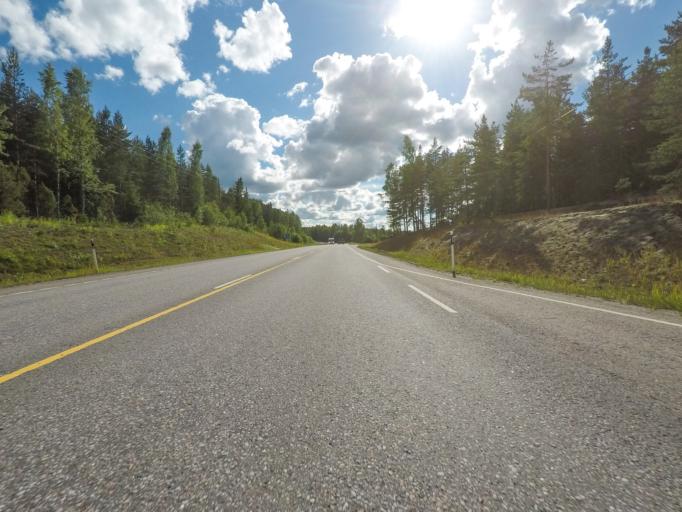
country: FI
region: Uusimaa
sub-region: Helsinki
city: Nurmijaervi
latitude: 60.5215
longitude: 24.6596
